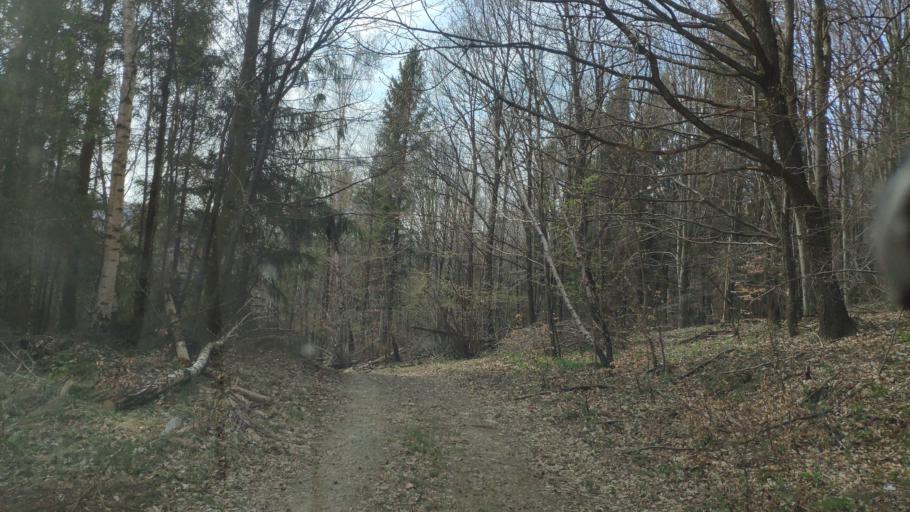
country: SK
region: Kosicky
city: Moldava nad Bodvou
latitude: 48.7433
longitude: 21.0362
